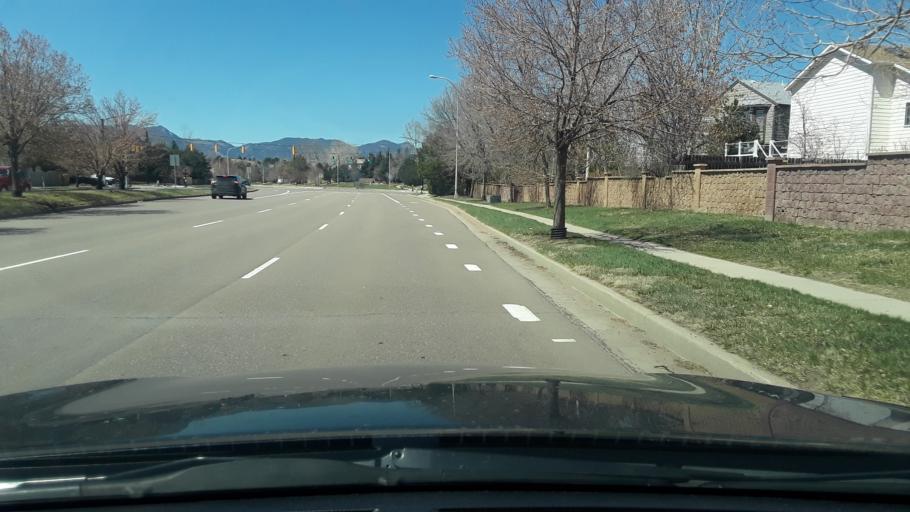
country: US
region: Colorado
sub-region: El Paso County
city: Black Forest
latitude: 38.9565
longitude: -104.7487
